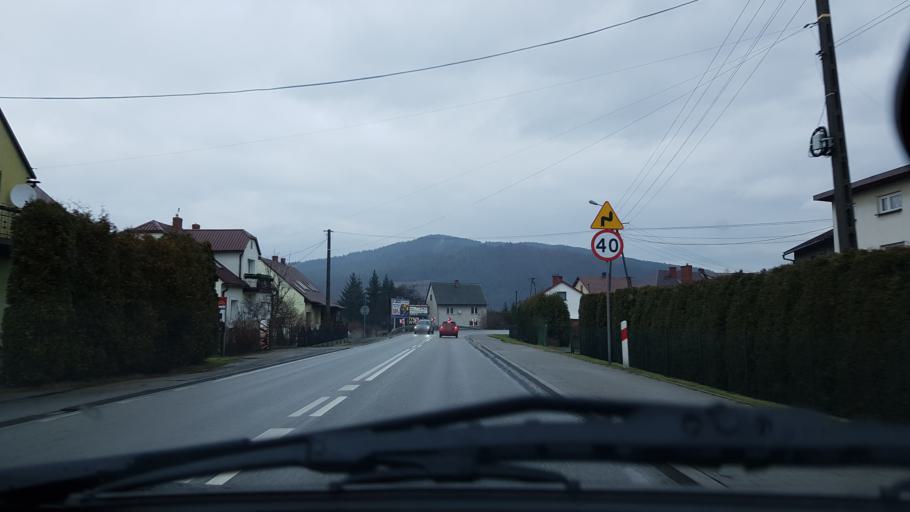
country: PL
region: Lesser Poland Voivodeship
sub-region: Powiat suski
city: Stryszawa
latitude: 49.7348
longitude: 19.5287
